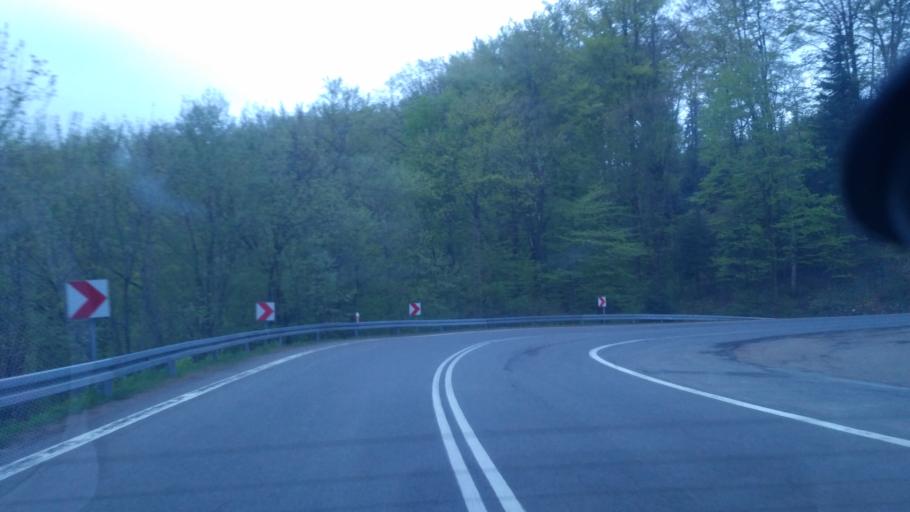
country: PL
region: Subcarpathian Voivodeship
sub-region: Powiat sanocki
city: Tyrawa Woloska
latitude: 49.5568
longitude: 22.3368
